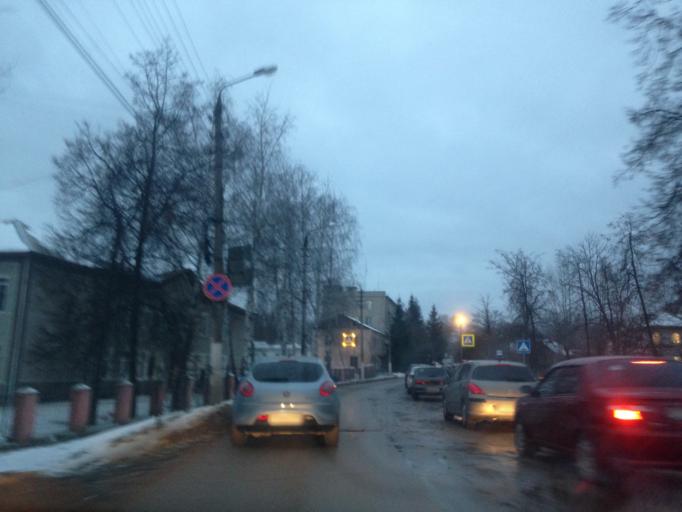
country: RU
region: Tula
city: Shchekino
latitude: 53.9980
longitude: 37.5131
